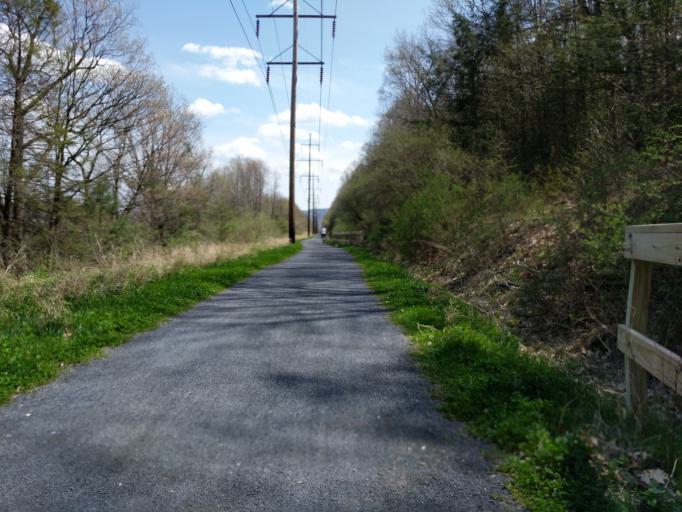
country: US
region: New York
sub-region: Tompkins County
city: Northwest Ithaca
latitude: 42.4675
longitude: -76.5275
